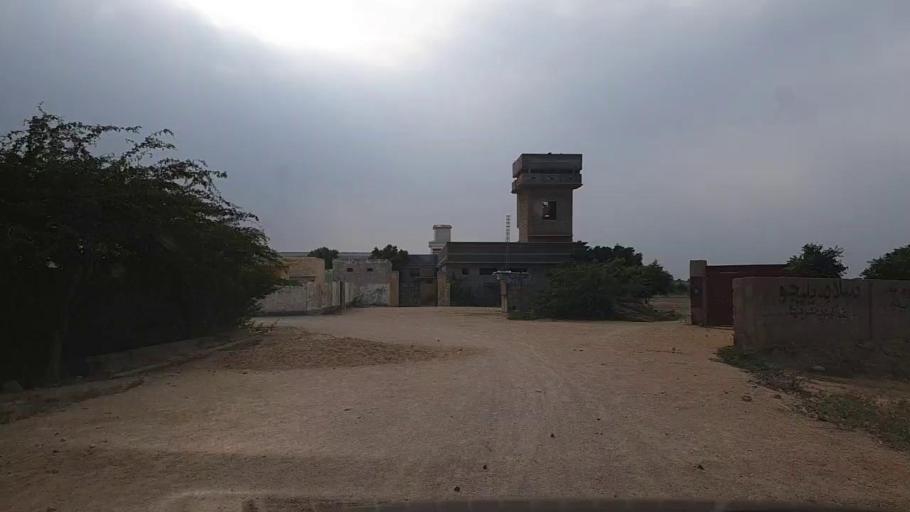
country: PK
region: Sindh
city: Thatta
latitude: 24.8451
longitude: 67.7745
